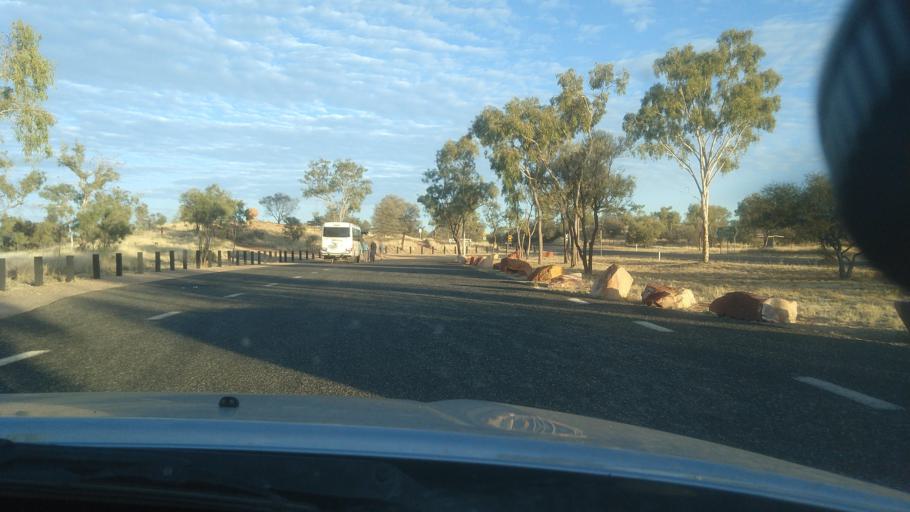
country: AU
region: Northern Territory
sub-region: Alice Springs
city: Alice Springs
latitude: -23.6981
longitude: 133.8202
